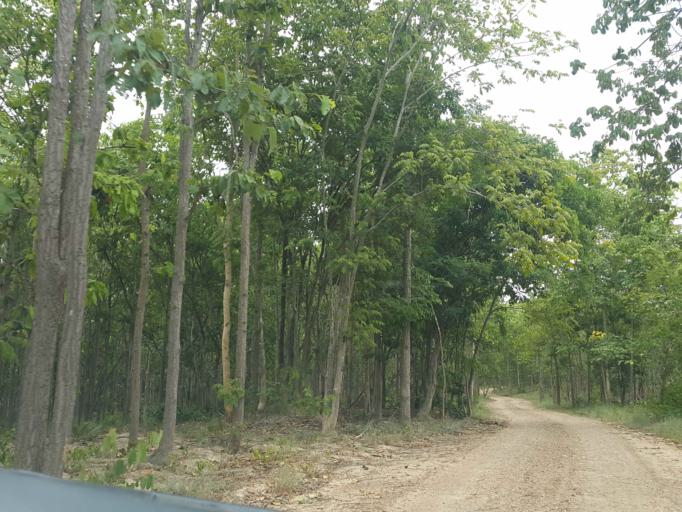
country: TH
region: Chiang Mai
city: Doi Lo
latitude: 18.5029
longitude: 98.7405
